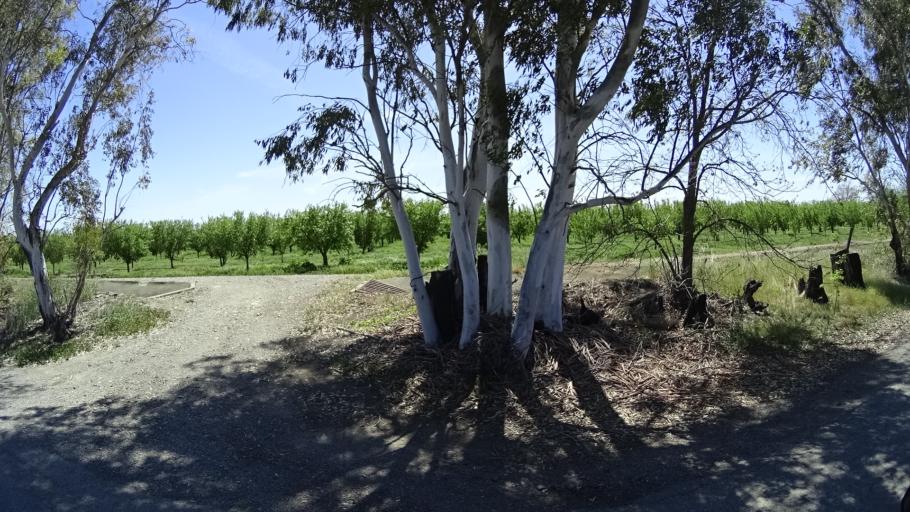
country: US
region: California
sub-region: Glenn County
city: Orland
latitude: 39.7322
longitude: -122.1100
